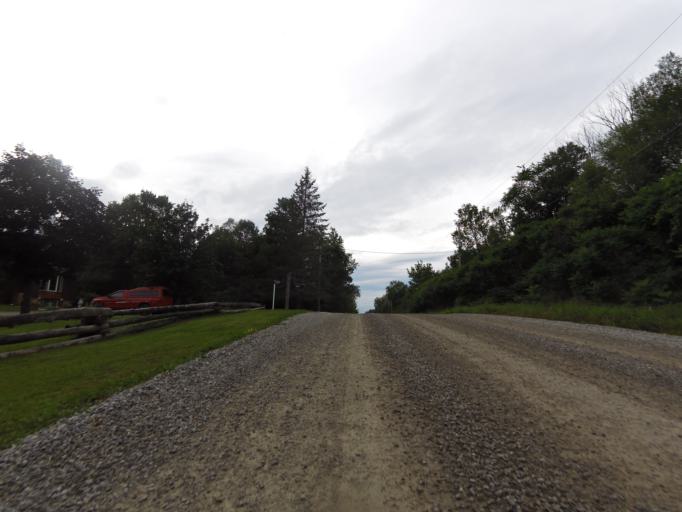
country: CA
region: Ontario
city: Carleton Place
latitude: 45.1465
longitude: -76.2279
